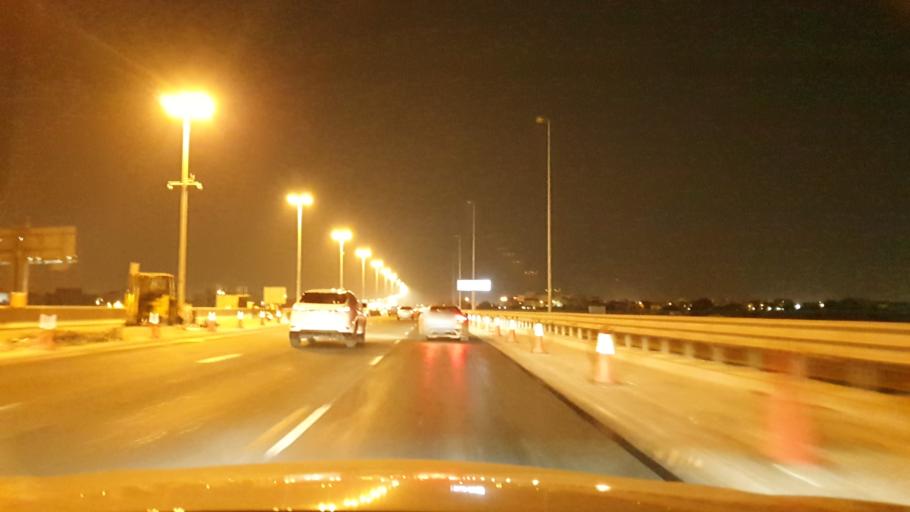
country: BH
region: Manama
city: Jidd Hafs
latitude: 26.2034
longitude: 50.5129
